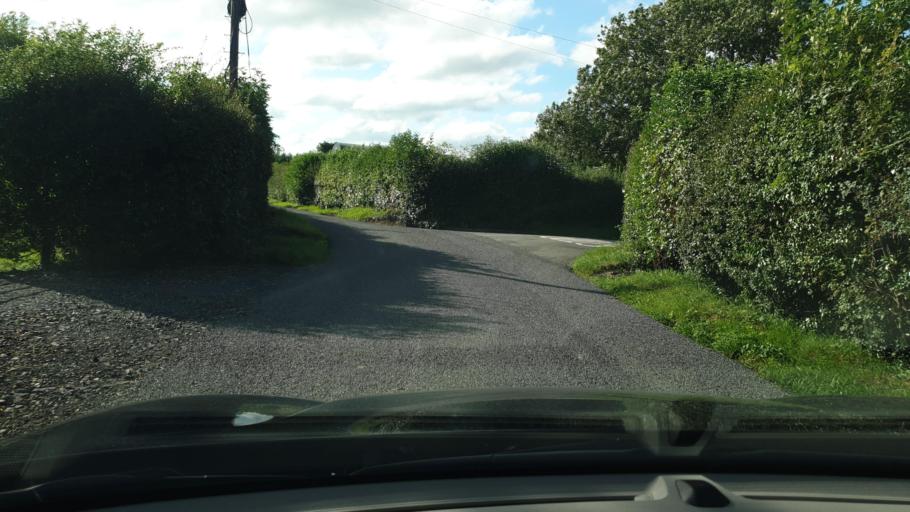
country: IE
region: Leinster
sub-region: An Mhi
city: Ashbourne
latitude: 53.5827
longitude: -6.3522
